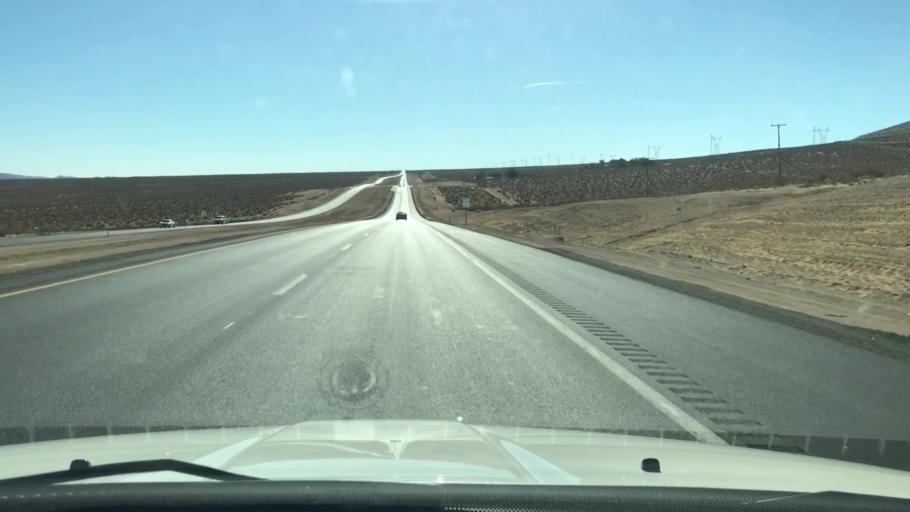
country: US
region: California
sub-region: Kern County
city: Inyokern
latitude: 35.6225
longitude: -117.8859
